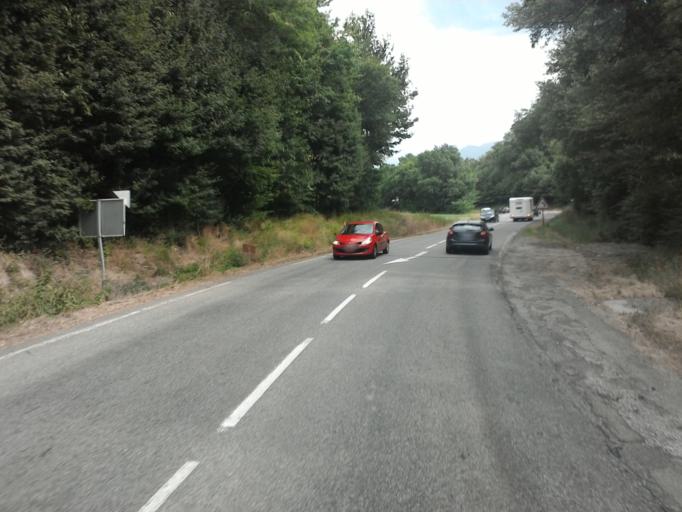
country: FR
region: Rhone-Alpes
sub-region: Departement de l'Isere
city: La Mure
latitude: 44.9008
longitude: 5.8004
